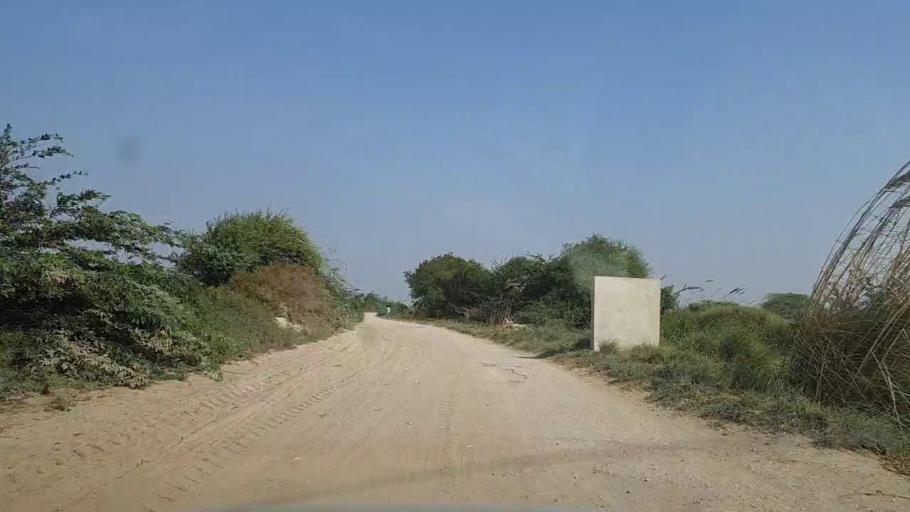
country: PK
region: Sindh
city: Mirpur Sakro
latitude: 24.5597
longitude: 67.6033
